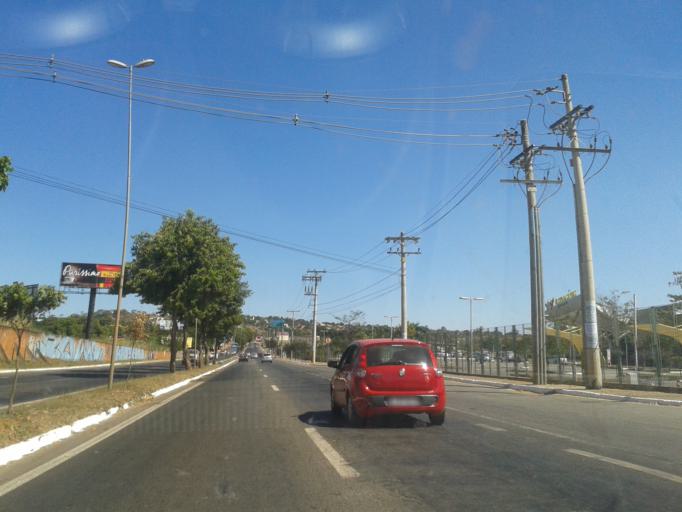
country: BR
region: Goias
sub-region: Goiania
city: Goiania
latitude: -16.6314
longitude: -49.2777
